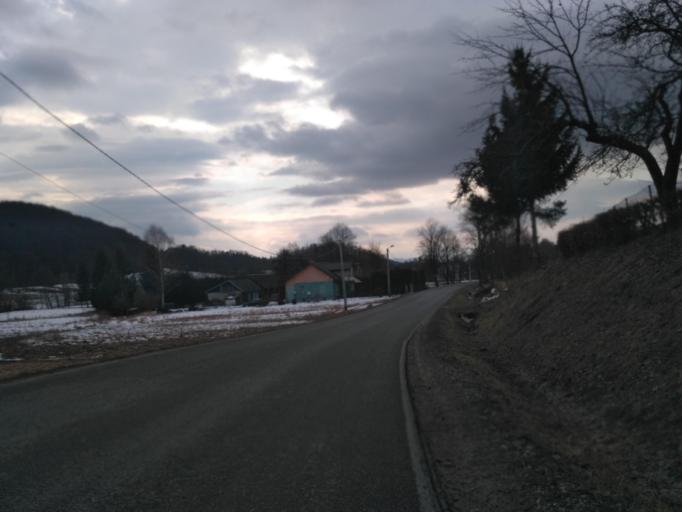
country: PL
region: Subcarpathian Voivodeship
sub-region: Powiat sanocki
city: Strachocina
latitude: 49.6199
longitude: 22.1529
